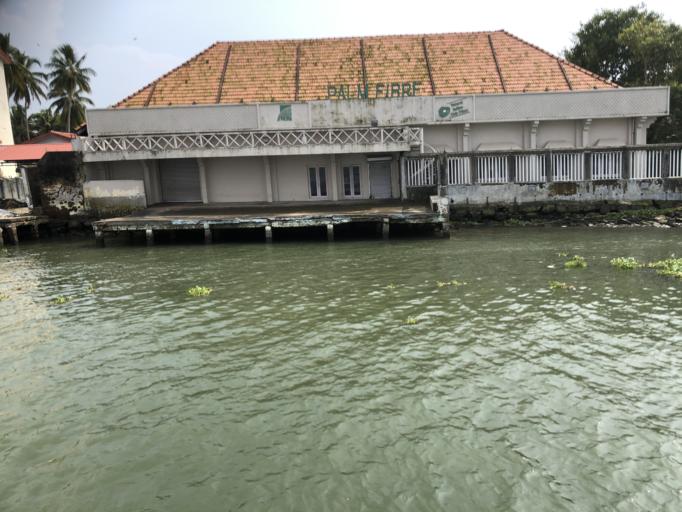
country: IN
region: Kerala
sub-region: Ernakulam
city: Cochin
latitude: 9.9694
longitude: 76.2469
